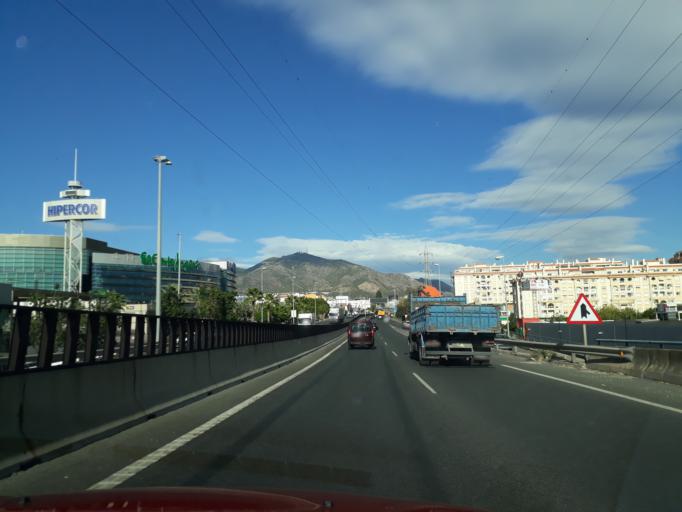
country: ES
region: Andalusia
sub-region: Provincia de Malaga
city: Fuengirola
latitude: 36.5464
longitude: -4.6323
